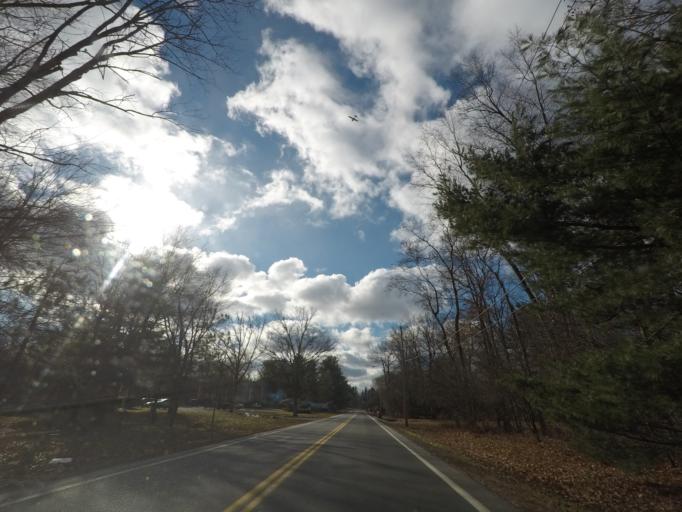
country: US
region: New York
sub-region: Schenectady County
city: East Glenville
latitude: 42.8834
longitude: -73.8837
